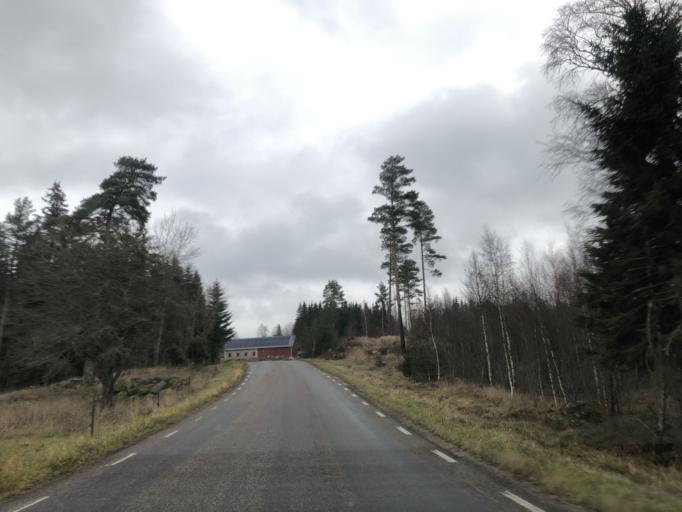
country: SE
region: Vaestra Goetaland
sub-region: Ulricehamns Kommun
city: Ulricehamn
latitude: 57.8701
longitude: 13.5455
